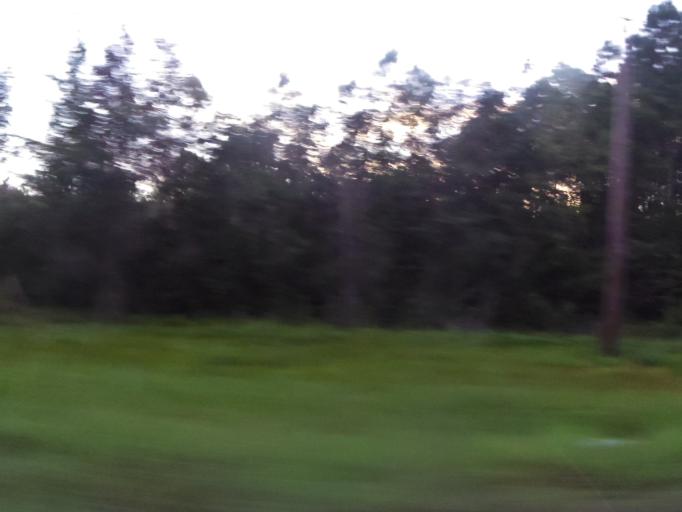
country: US
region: Georgia
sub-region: Camden County
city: Kingsland
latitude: 30.8194
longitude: -81.6942
